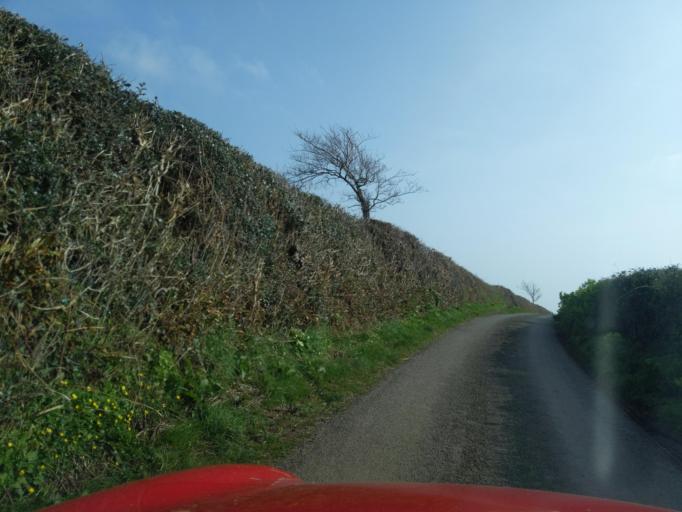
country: GB
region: England
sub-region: Devon
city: Kingsbridge
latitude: 50.2909
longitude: -3.7354
